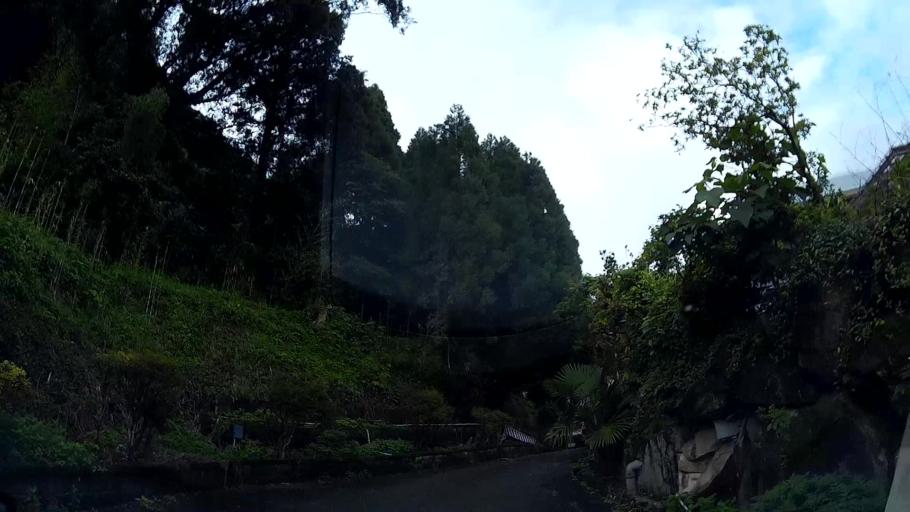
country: JP
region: Kumamoto
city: Ozu
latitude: 32.8788
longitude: 130.9571
